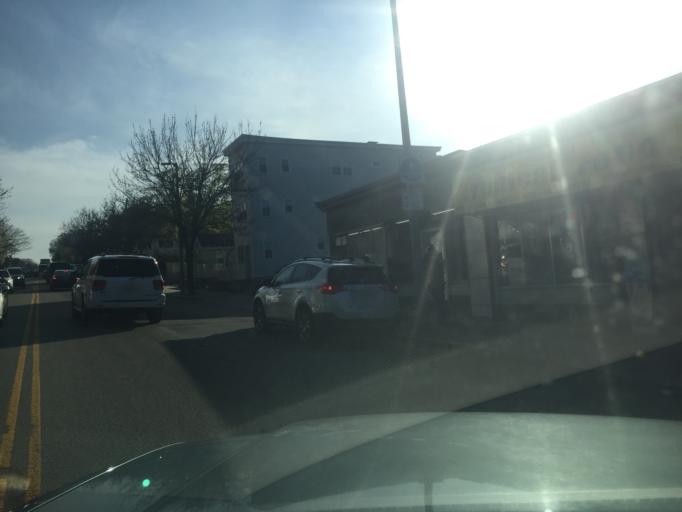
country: US
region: Massachusetts
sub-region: Suffolk County
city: Jamaica Plain
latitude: 42.2783
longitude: -71.1371
